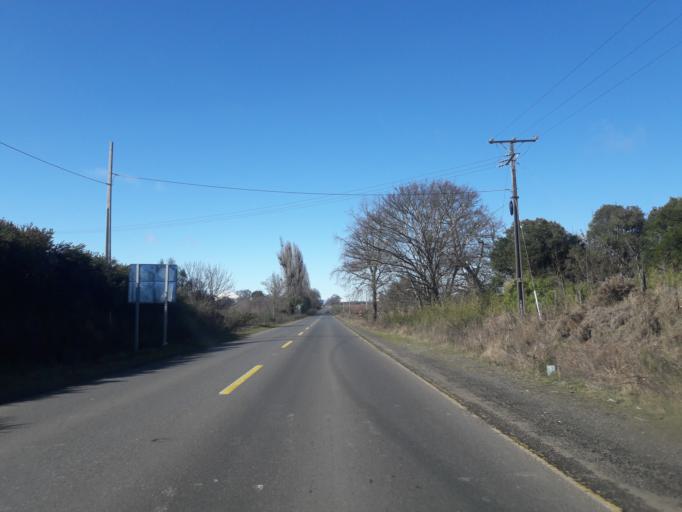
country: CL
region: Araucania
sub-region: Provincia de Malleco
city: Victoria
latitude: -38.2581
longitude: -72.2625
